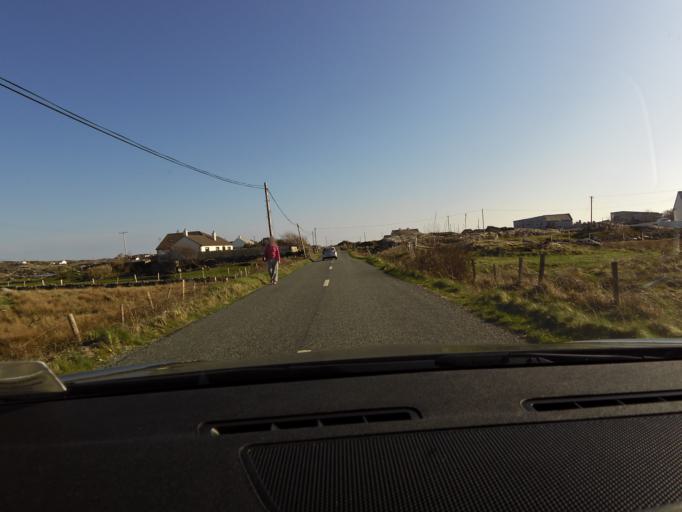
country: IE
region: Connaught
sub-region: County Galway
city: Clifden
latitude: 53.4011
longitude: -10.0310
